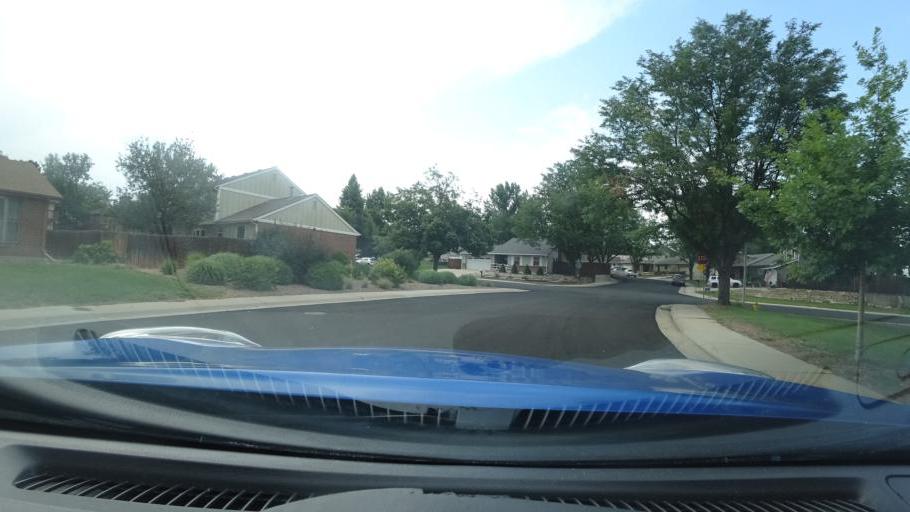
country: US
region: Colorado
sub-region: Adams County
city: Aurora
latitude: 39.6899
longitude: -104.8140
